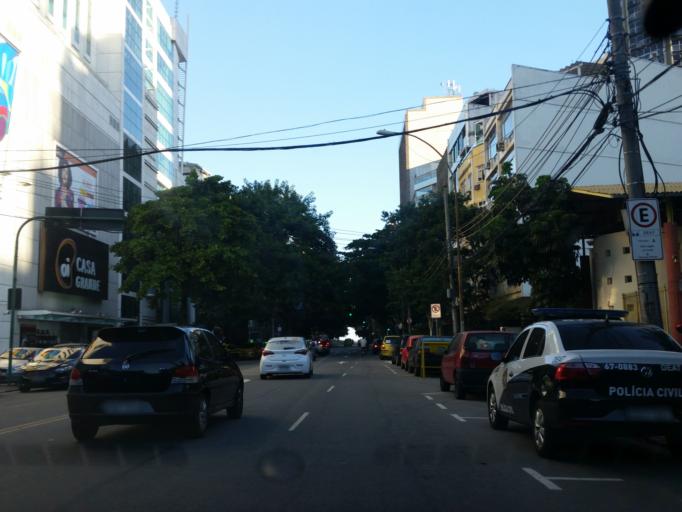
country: BR
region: Rio de Janeiro
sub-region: Rio De Janeiro
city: Rio de Janeiro
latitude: -22.9819
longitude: -43.2181
